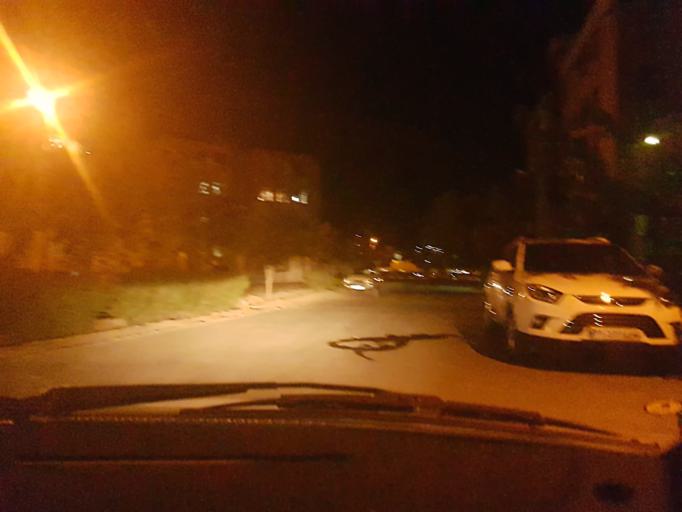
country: IR
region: Markazi
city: Arak
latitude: 34.0700
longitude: 49.6767
